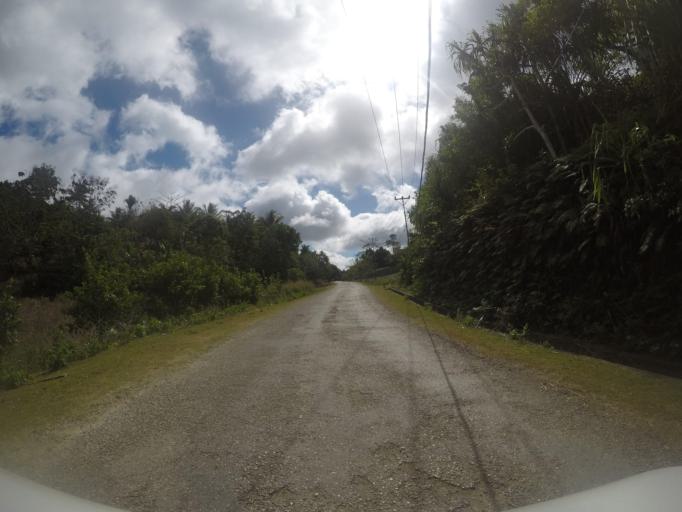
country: TL
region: Lautem
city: Lospalos
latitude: -8.5433
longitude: 126.9458
